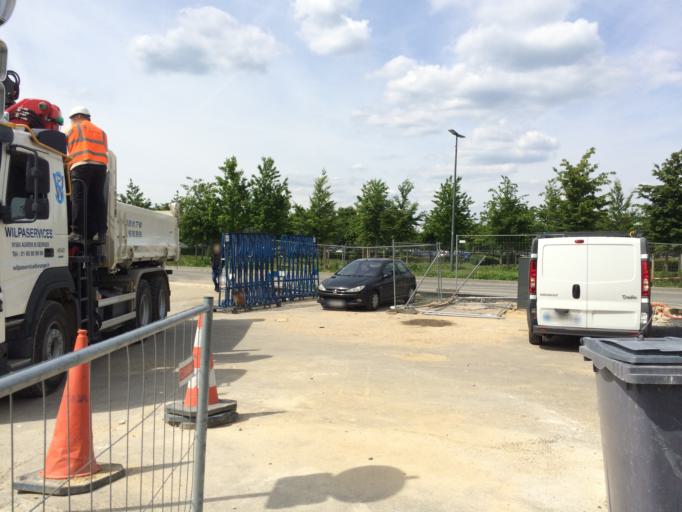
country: FR
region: Ile-de-France
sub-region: Departement de l'Essonne
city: Vauhallan
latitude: 48.7142
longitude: 2.2009
